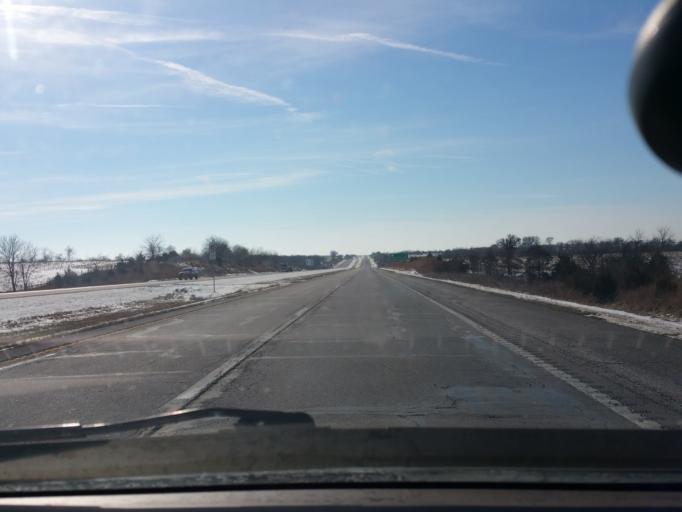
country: US
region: Iowa
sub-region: Decatur County
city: Lamoni
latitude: 40.4541
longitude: -93.9807
